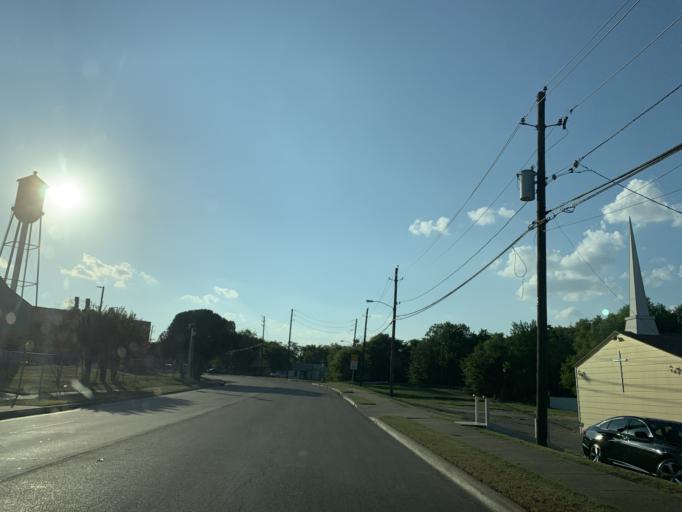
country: US
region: Texas
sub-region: Dallas County
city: Dallas
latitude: 32.6975
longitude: -96.7868
